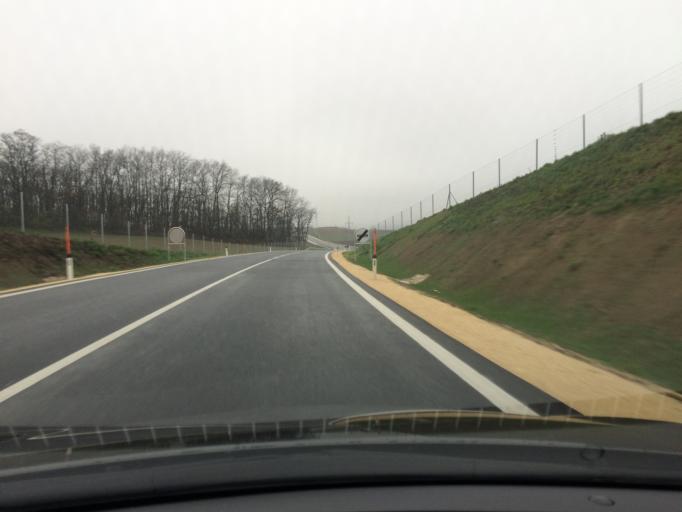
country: AT
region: Lower Austria
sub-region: Politischer Bezirk Mistelbach
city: Mistelbach
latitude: 48.5467
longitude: 16.5758
